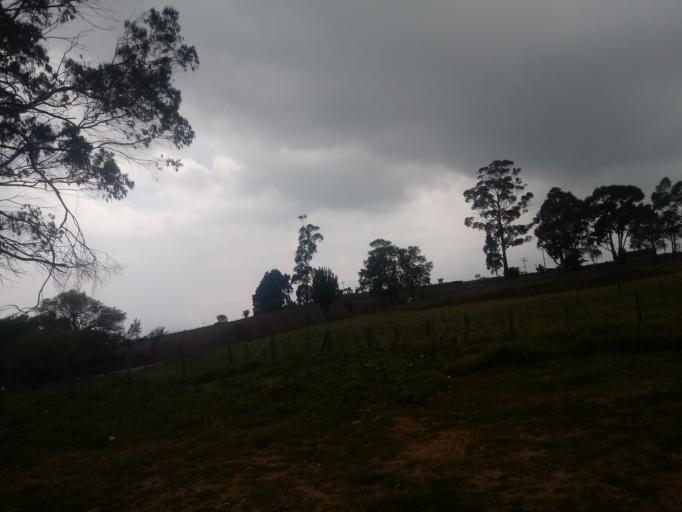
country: CR
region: Cartago
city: Cot
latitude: 9.9318
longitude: -83.8828
